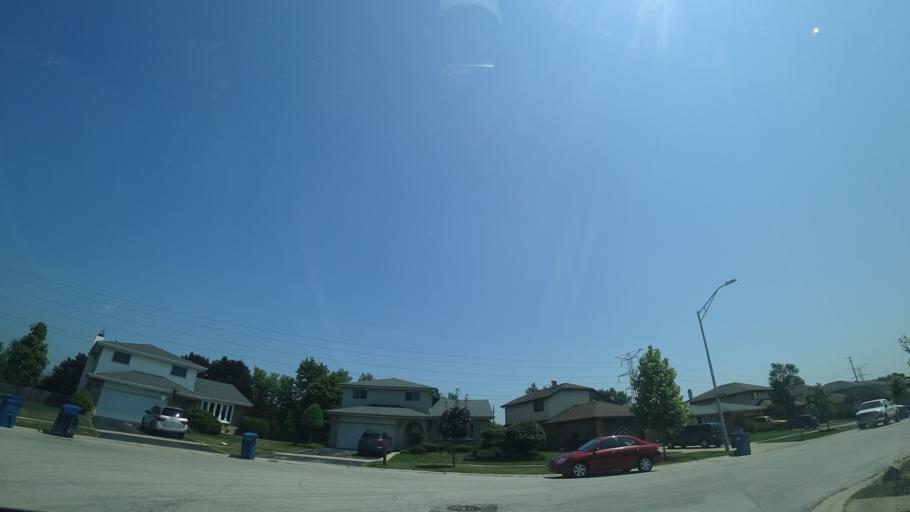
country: US
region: Illinois
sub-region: Cook County
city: Alsip
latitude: 41.6879
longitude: -87.7420
